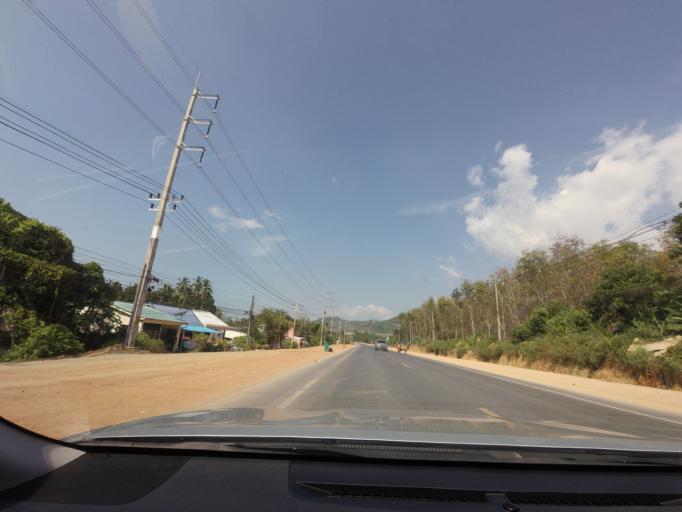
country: TH
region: Phangnga
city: Ban Khao Lak
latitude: 8.6978
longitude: 98.2568
